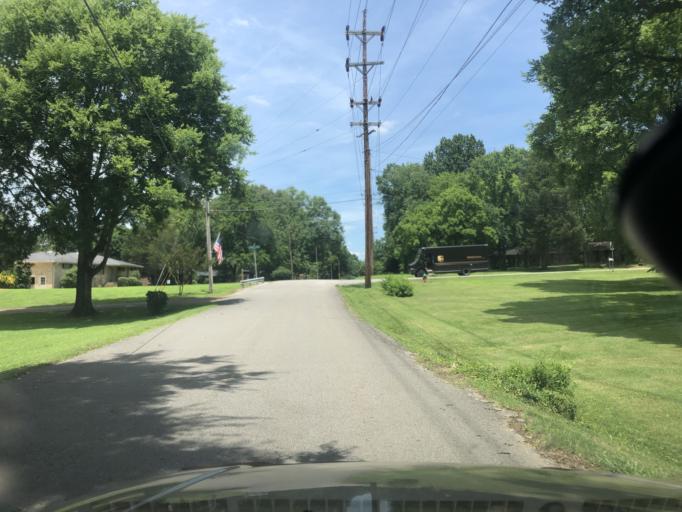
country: US
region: Tennessee
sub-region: Davidson County
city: Lakewood
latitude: 36.2469
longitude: -86.7003
